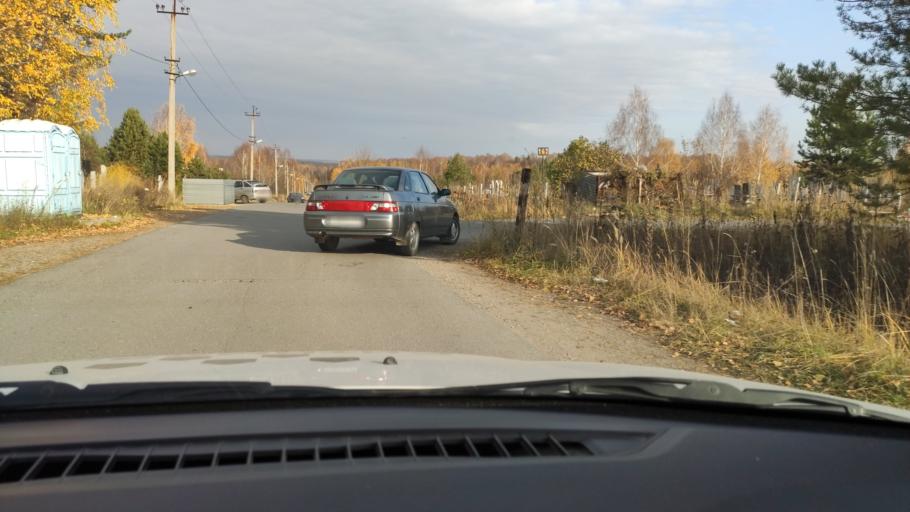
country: RU
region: Perm
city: Kondratovo
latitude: 58.0654
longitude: 56.1441
